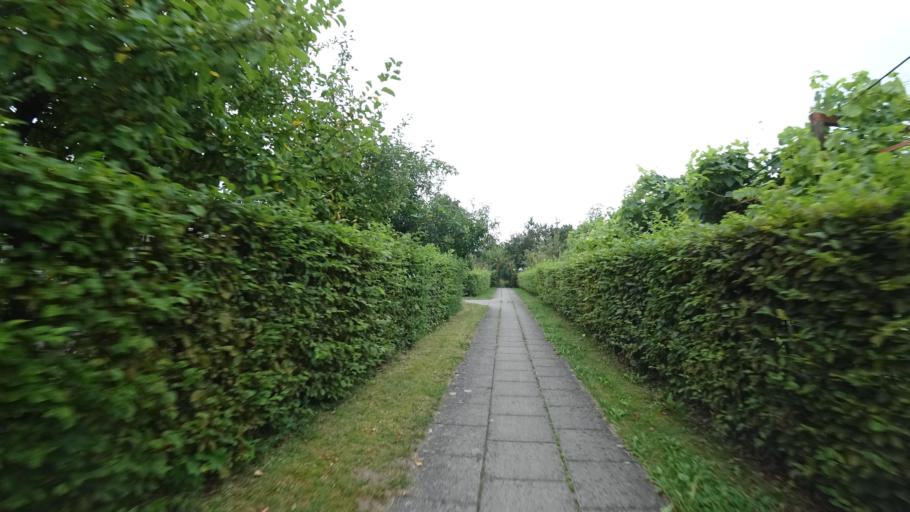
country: DE
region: North Rhine-Westphalia
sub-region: Regierungsbezirk Detmold
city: Guetersloh
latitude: 51.9169
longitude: 8.4149
